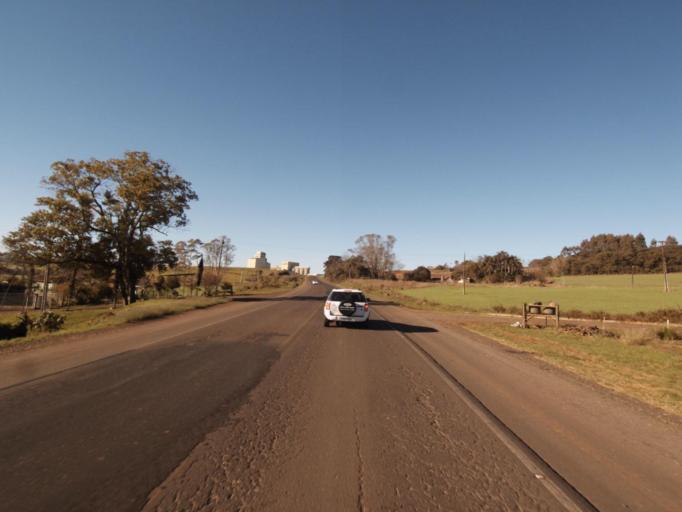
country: BR
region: Rio Grande do Sul
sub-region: Frederico Westphalen
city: Frederico Westphalen
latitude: -26.9008
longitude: -53.1902
